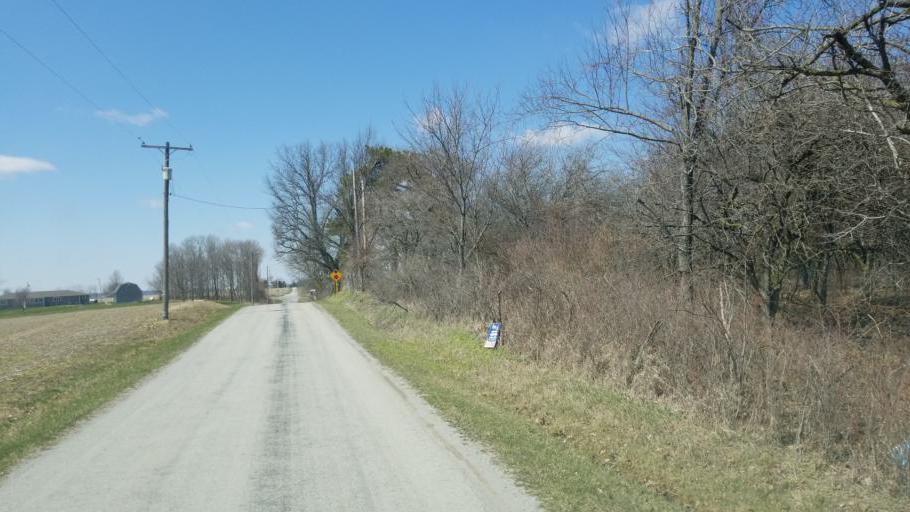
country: US
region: Ohio
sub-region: Marion County
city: Marion
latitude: 40.7244
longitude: -83.1465
